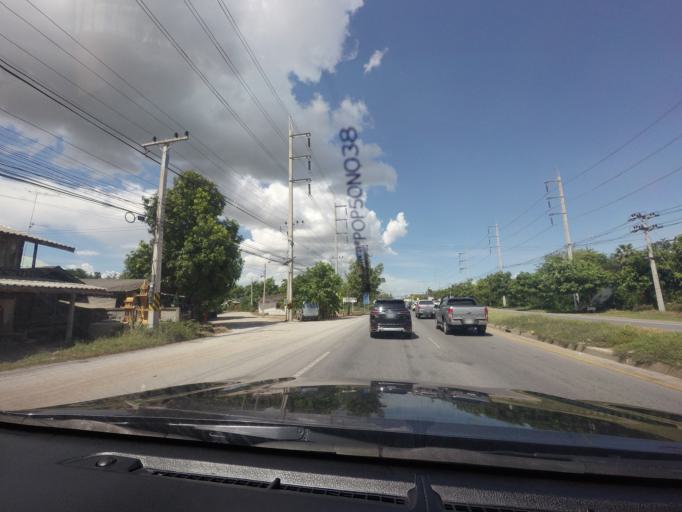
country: TH
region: Kanchanaburi
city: Phanom Thuan
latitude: 14.1009
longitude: 99.6577
